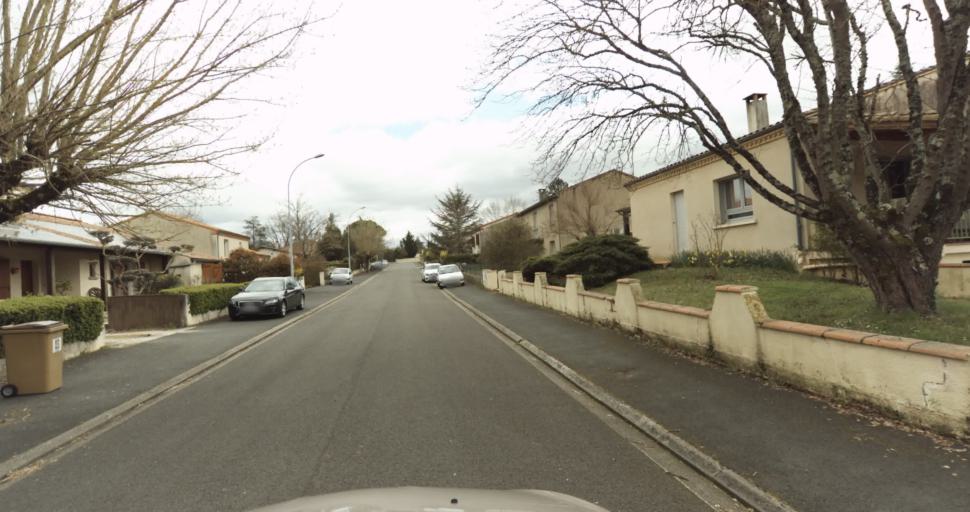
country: FR
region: Midi-Pyrenees
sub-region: Departement du Tarn
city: Puygouzon
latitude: 43.8862
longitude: 2.1683
